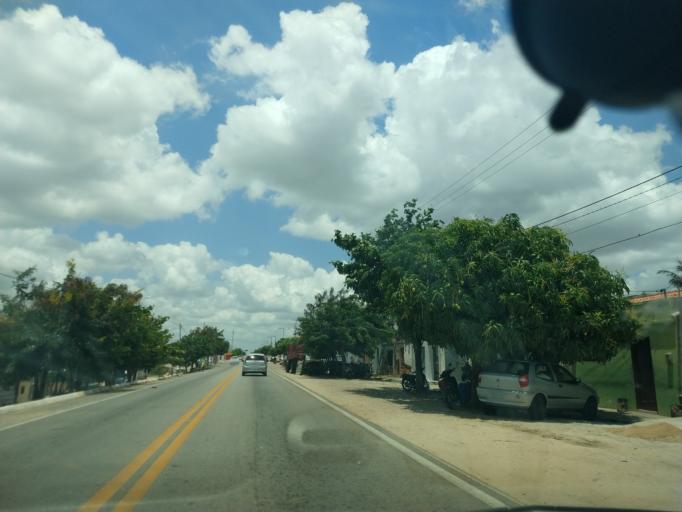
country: BR
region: Rio Grande do Norte
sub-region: Tangara
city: Tangara
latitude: -6.1966
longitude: -35.7974
